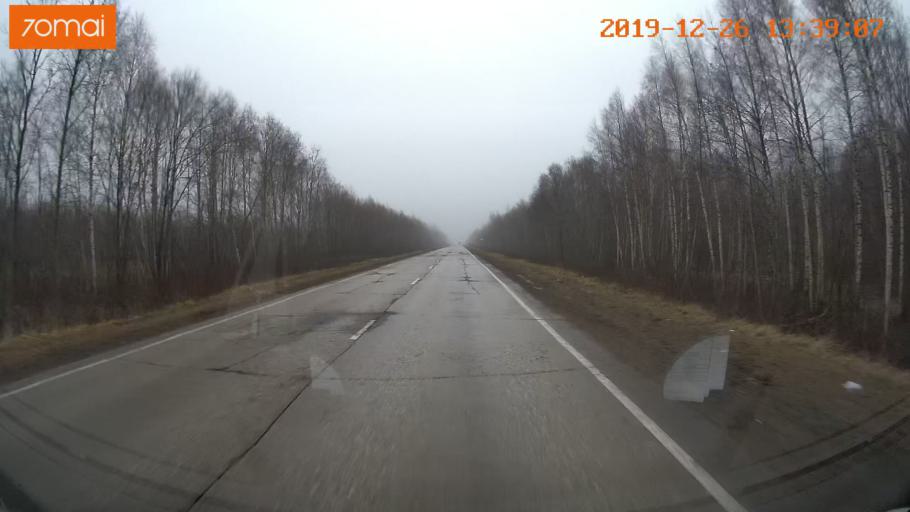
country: RU
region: Vologda
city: Sheksna
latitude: 58.7552
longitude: 38.4051
